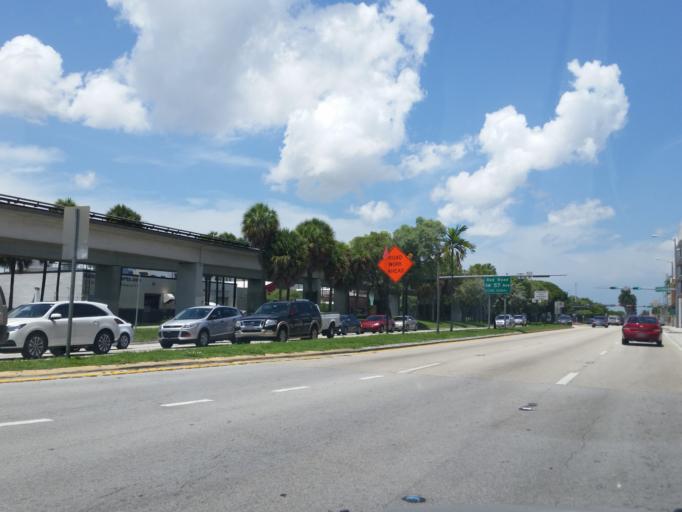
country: US
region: Florida
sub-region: Miami-Dade County
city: South Miami
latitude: 25.7060
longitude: -80.2874
